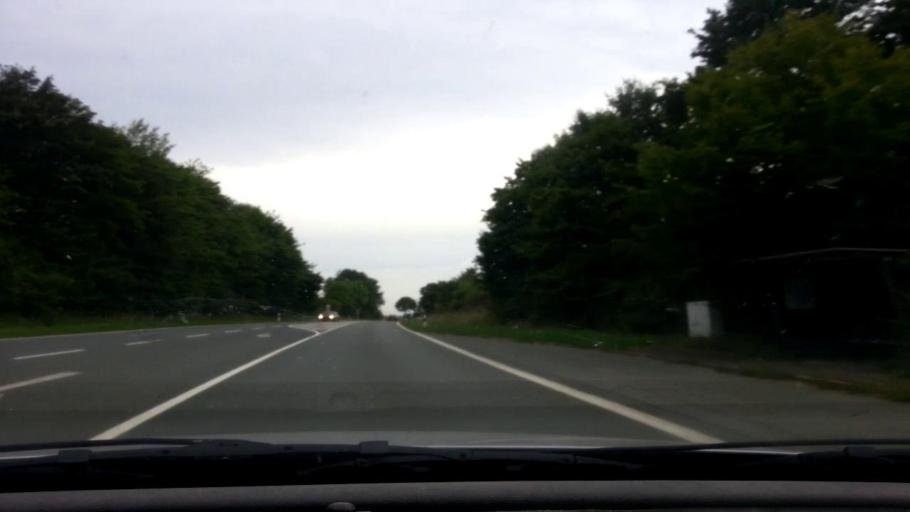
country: DE
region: Bavaria
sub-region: Upper Franconia
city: Emtmannsberg
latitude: 49.9104
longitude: 11.6604
